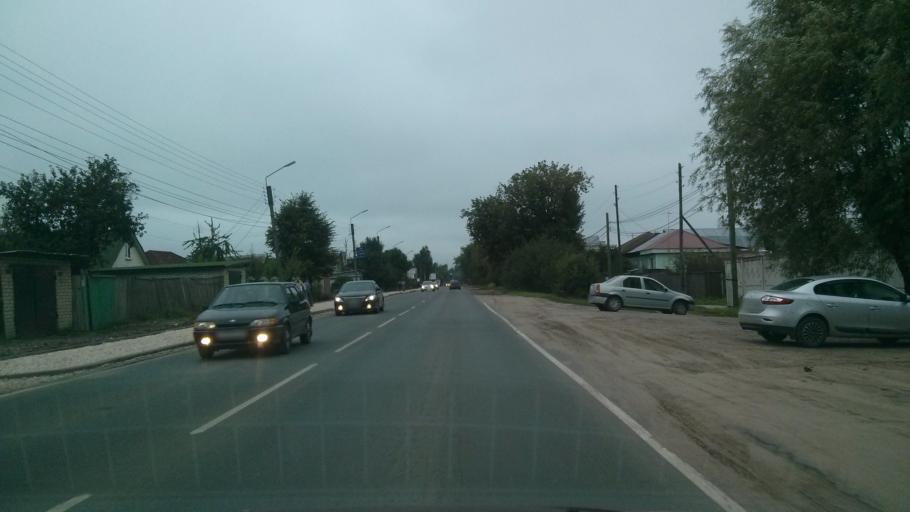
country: RU
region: Vladimir
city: Murom
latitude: 55.5911
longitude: 42.0350
